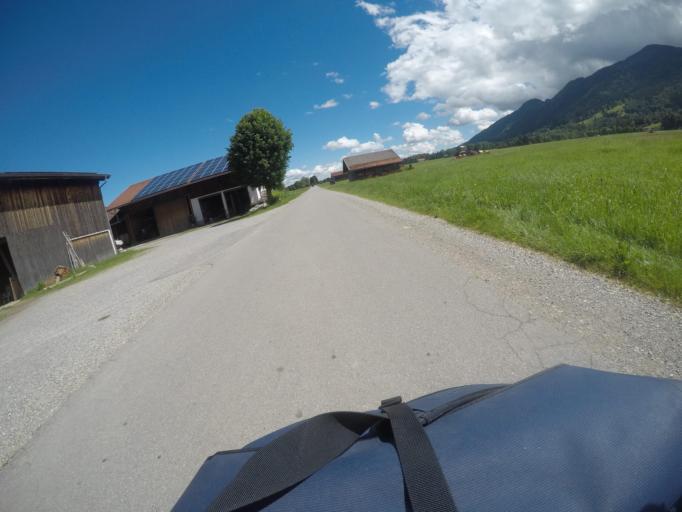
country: DE
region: Bavaria
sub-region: Swabia
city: Halblech
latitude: 47.6253
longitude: 10.8055
